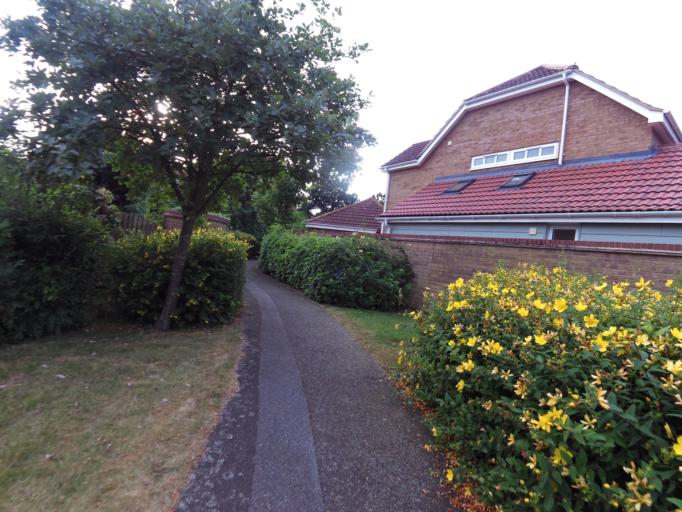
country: GB
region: England
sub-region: Suffolk
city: Ipswich
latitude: 52.0700
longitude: 1.1714
